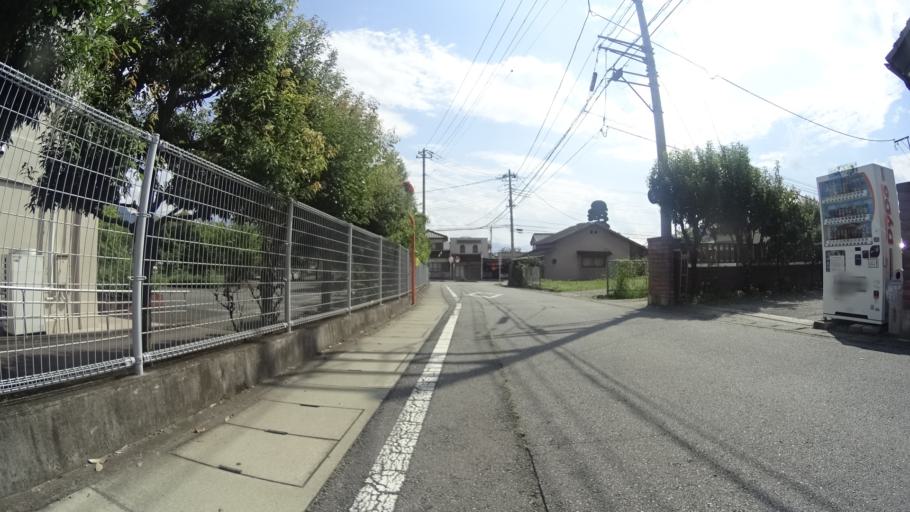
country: JP
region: Yamanashi
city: Enzan
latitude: 35.7092
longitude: 138.7318
